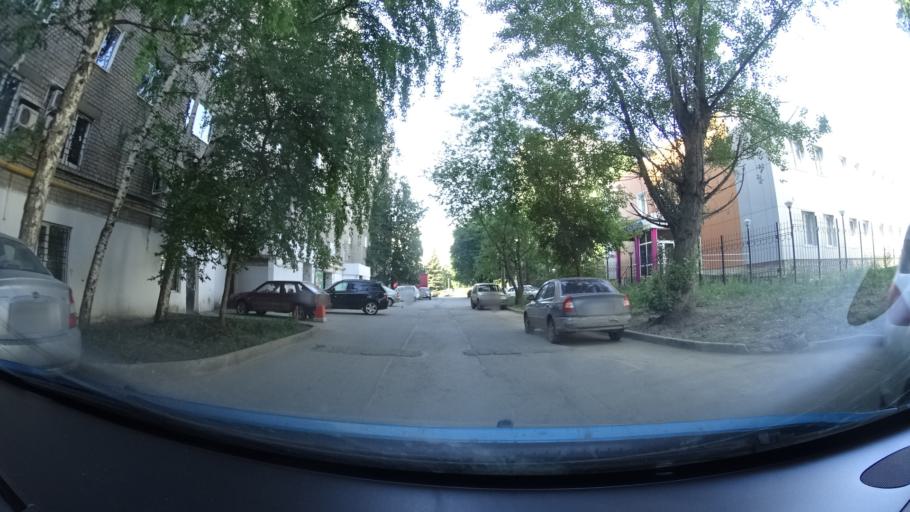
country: RU
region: Bashkortostan
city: Ufa
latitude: 54.7578
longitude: 55.9942
